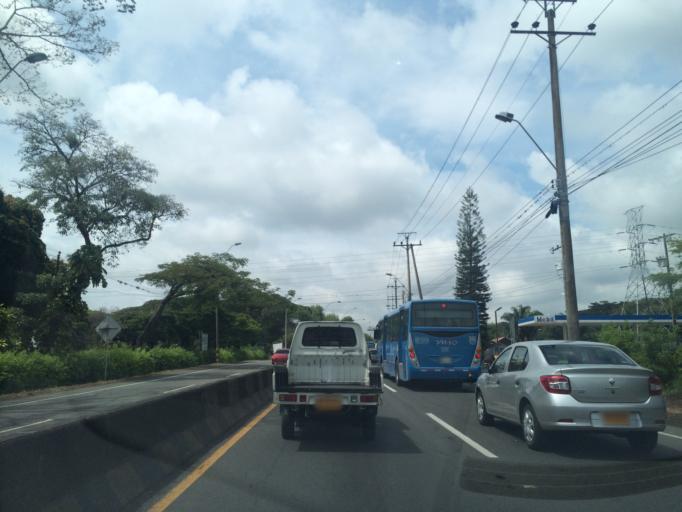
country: CO
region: Valle del Cauca
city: Cali
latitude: 3.3522
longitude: -76.5235
